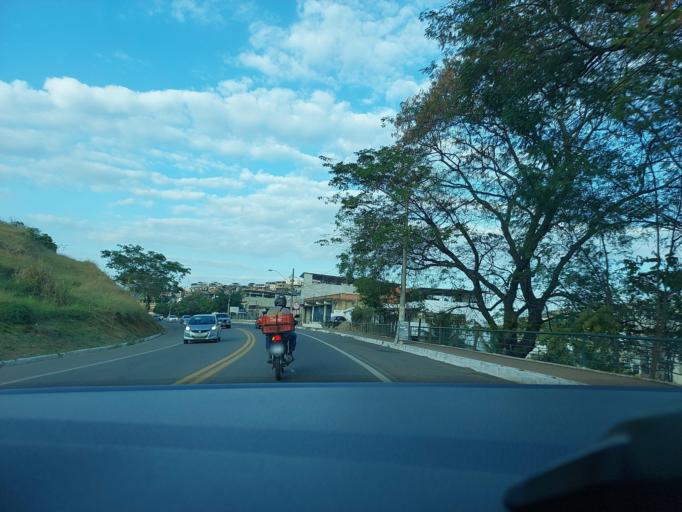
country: BR
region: Minas Gerais
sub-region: Muriae
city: Muriae
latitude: -21.1294
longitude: -42.3607
